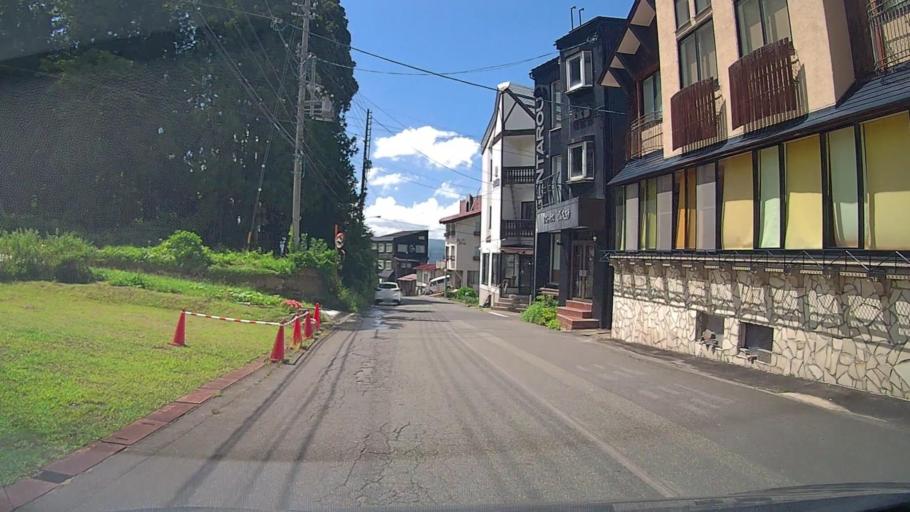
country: JP
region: Nagano
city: Iiyama
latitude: 36.9201
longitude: 138.4516
